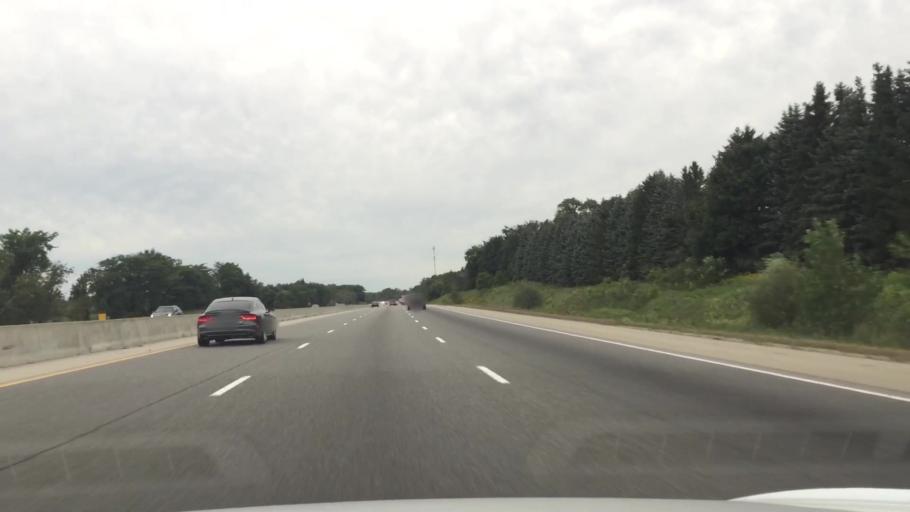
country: CA
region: Ontario
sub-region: Oxford County
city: Woodstock
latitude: 43.2106
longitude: -80.6118
